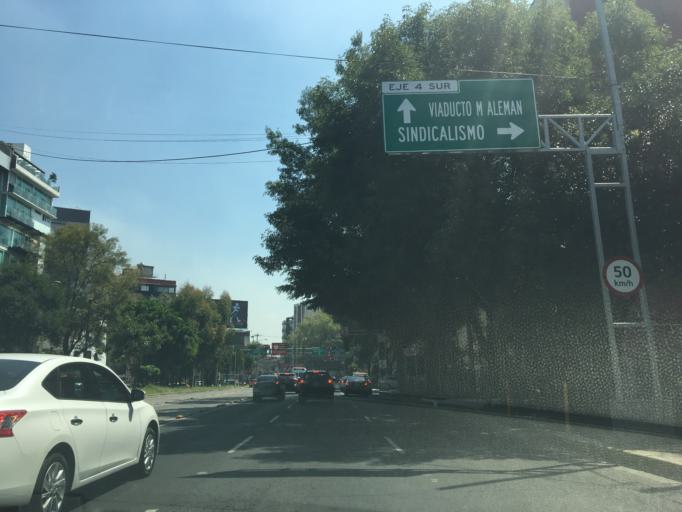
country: MX
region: Mexico City
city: Benito Juarez
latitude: 19.4039
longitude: -99.1726
